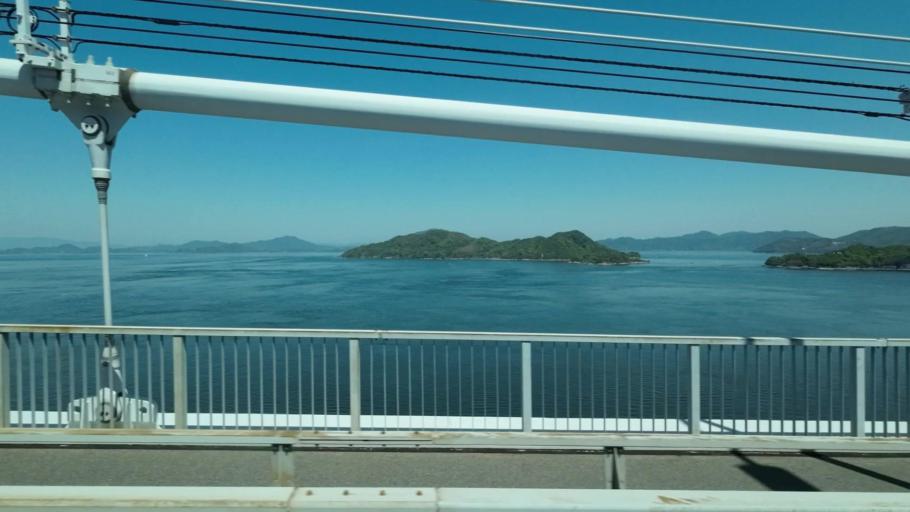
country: JP
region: Hiroshima
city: Takehara
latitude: 34.1260
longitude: 133.0116
